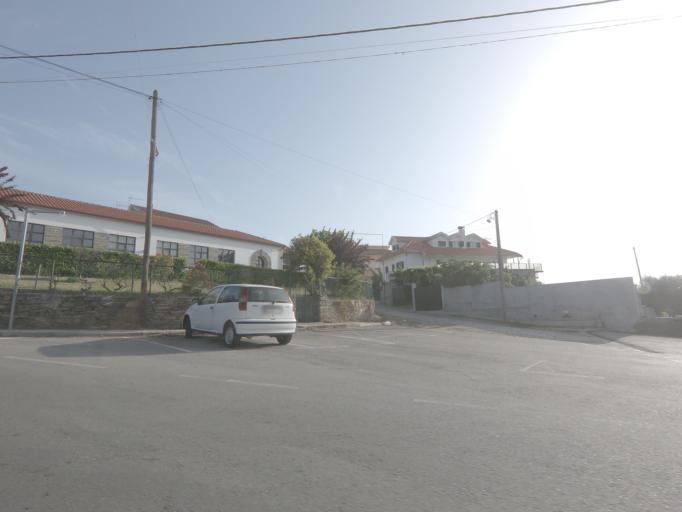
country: PT
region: Viseu
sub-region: Sao Joao da Pesqueira
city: Sao Joao da Pesqueira
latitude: 41.2276
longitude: -7.4673
